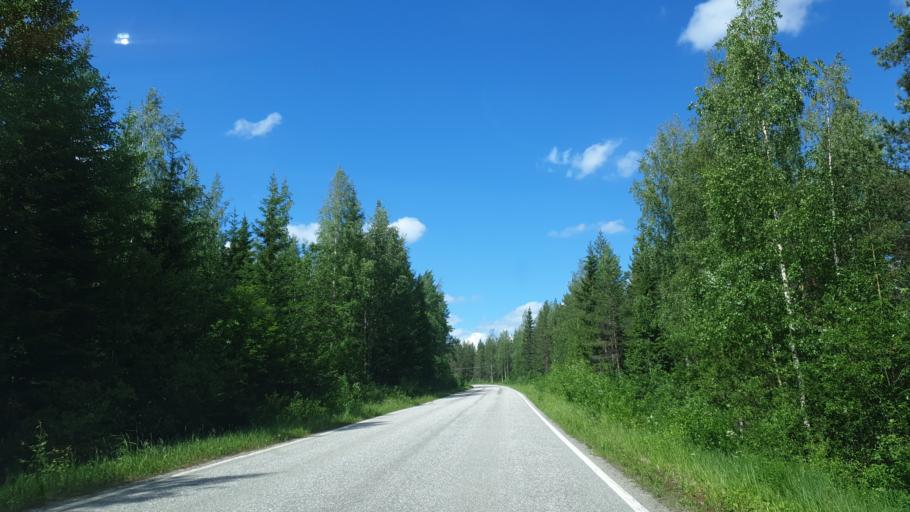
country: FI
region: Northern Savo
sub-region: Koillis-Savo
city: Kaavi
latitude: 63.0387
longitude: 28.5988
